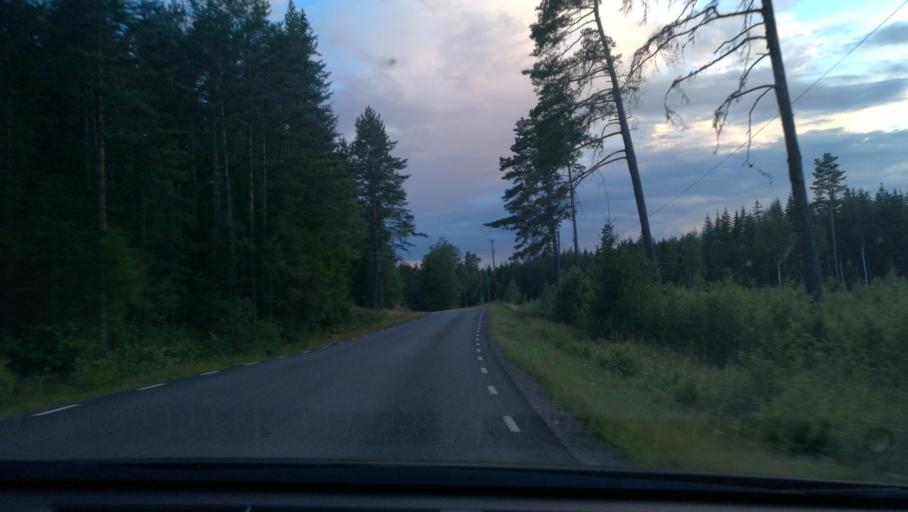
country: SE
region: OEstergoetland
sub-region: Norrkopings Kommun
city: Svartinge
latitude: 58.8188
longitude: 16.0321
